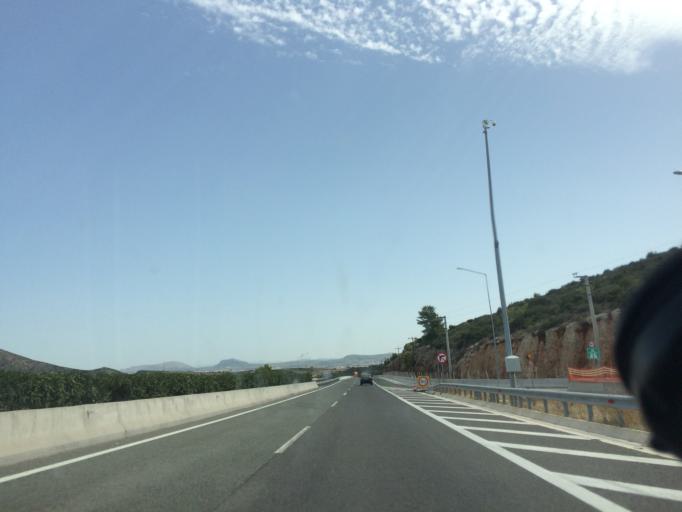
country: GR
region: Central Greece
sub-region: Nomos Voiotias
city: Akraifnia
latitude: 38.3918
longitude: 23.2393
